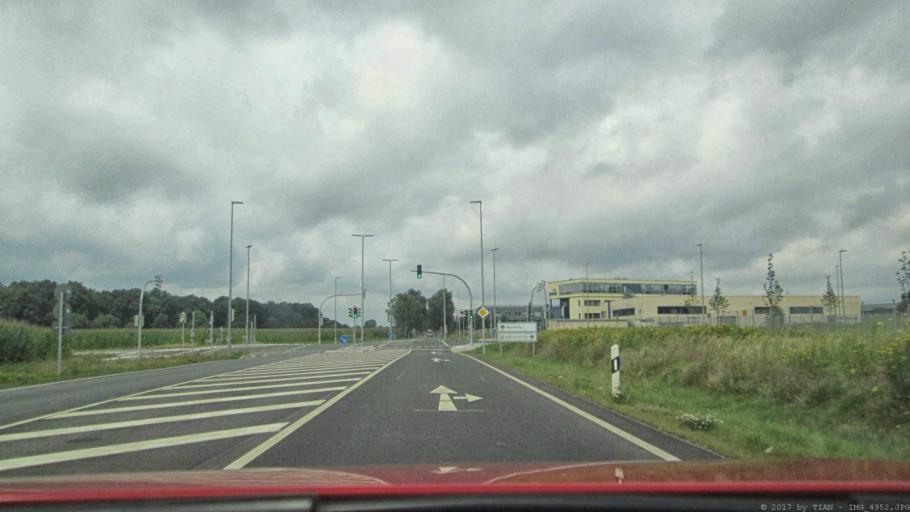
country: DE
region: Lower Saxony
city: Tappenbeck
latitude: 52.4519
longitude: 10.7615
